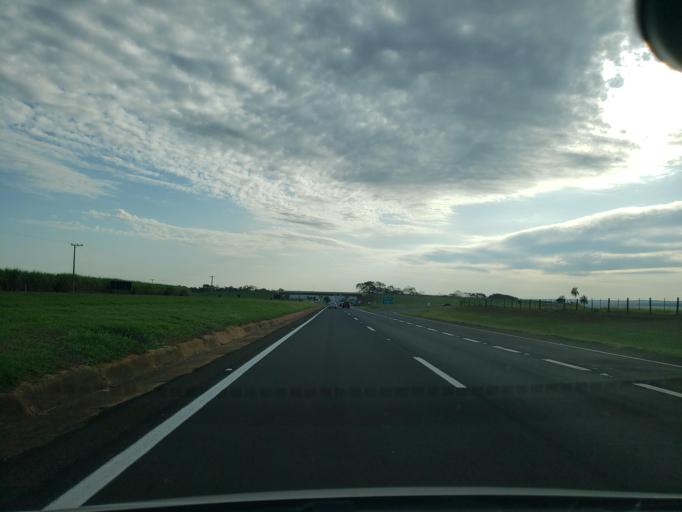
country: BR
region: Sao Paulo
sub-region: Guararapes
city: Guararapes
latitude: -21.2116
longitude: -50.7208
